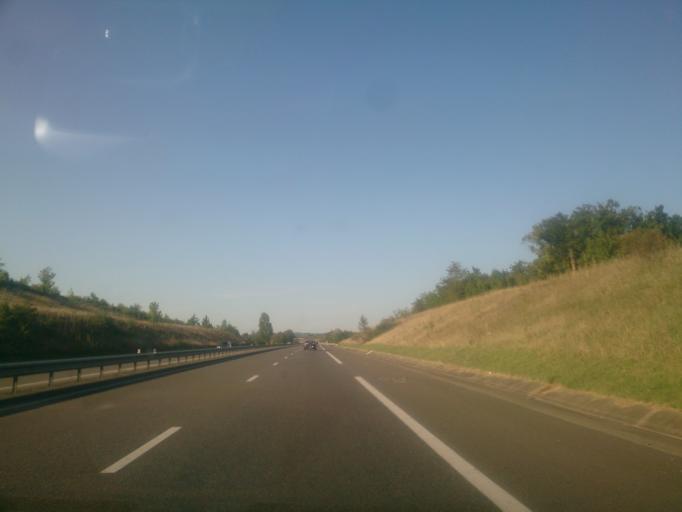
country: FR
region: Midi-Pyrenees
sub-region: Departement du Tarn-et-Garonne
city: Caussade
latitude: 44.1963
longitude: 1.5380
